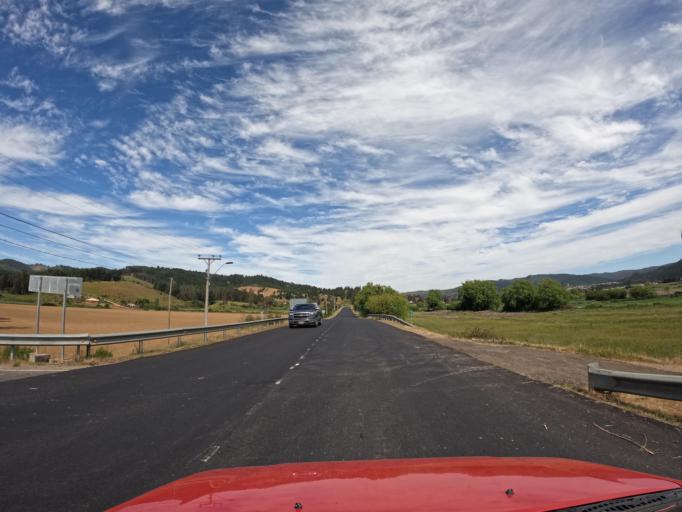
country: CL
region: Maule
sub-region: Provincia de Talca
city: Constitucion
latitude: -35.0768
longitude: -72.0242
